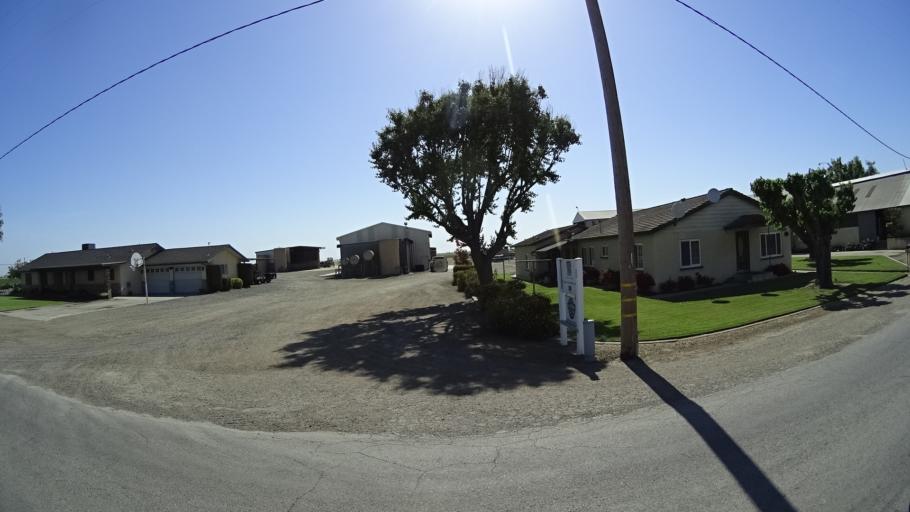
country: US
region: California
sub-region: Kings County
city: Home Garden
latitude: 36.2574
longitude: -119.5474
